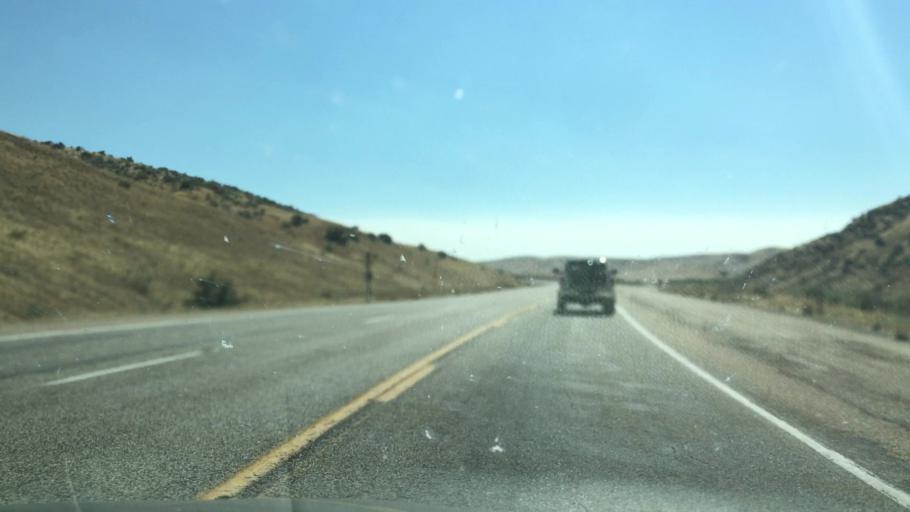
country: US
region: Idaho
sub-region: Ada County
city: Eagle
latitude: 43.8157
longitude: -116.2619
